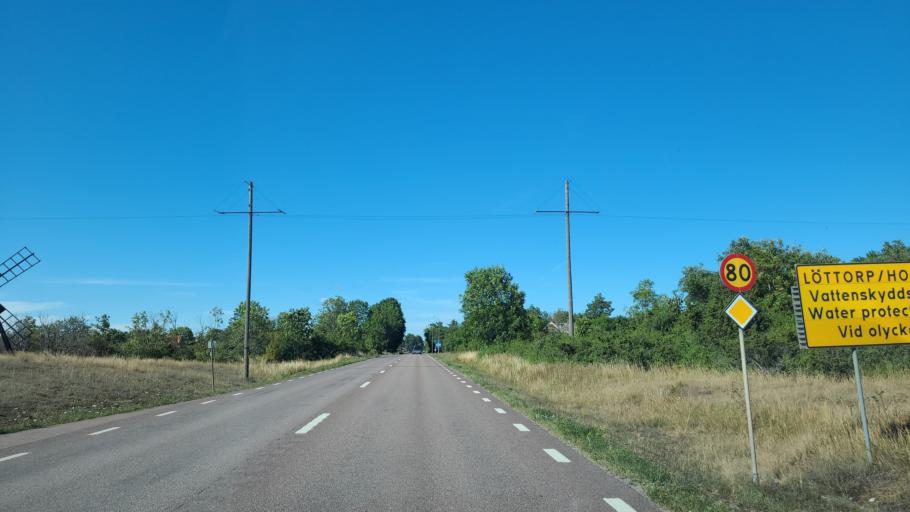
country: SE
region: Kalmar
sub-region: Borgholms Kommun
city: Borgholm
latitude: 57.1525
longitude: 17.0095
